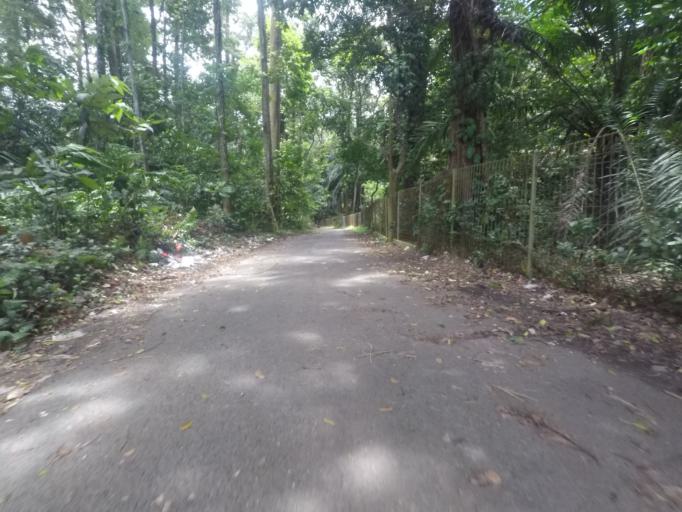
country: ID
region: West Java
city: Ciampea
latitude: -6.5540
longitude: 106.7539
